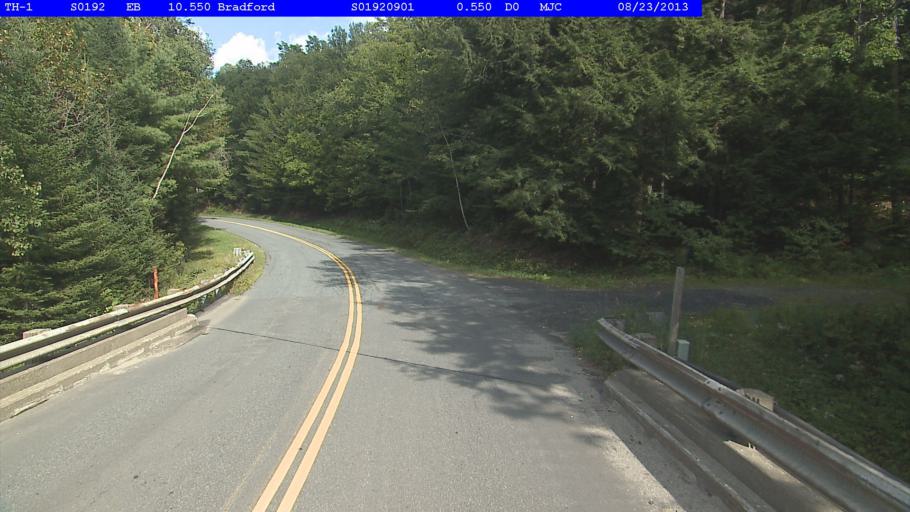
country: US
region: New Hampshire
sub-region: Grafton County
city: Orford
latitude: 44.0180
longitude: -72.2072
